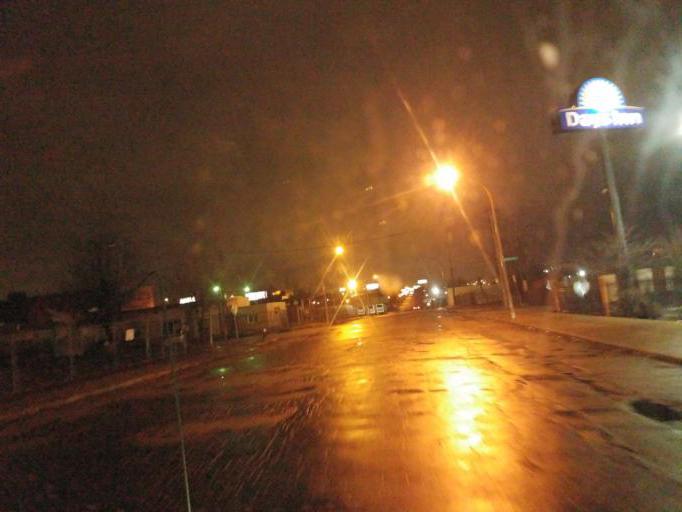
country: US
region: Missouri
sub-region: City of Saint Louis
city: St. Louis
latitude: 38.6534
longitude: -90.1923
